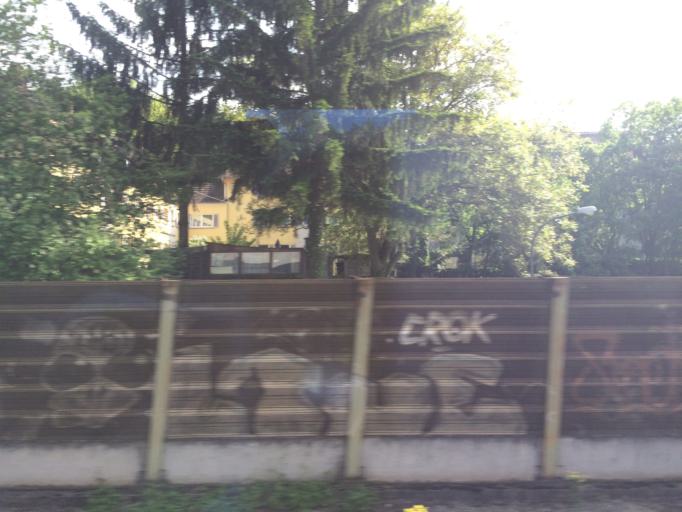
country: DE
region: Bavaria
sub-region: Regierungsbezirk Unterfranken
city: Wuerzburg
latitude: 49.7958
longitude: 9.9657
